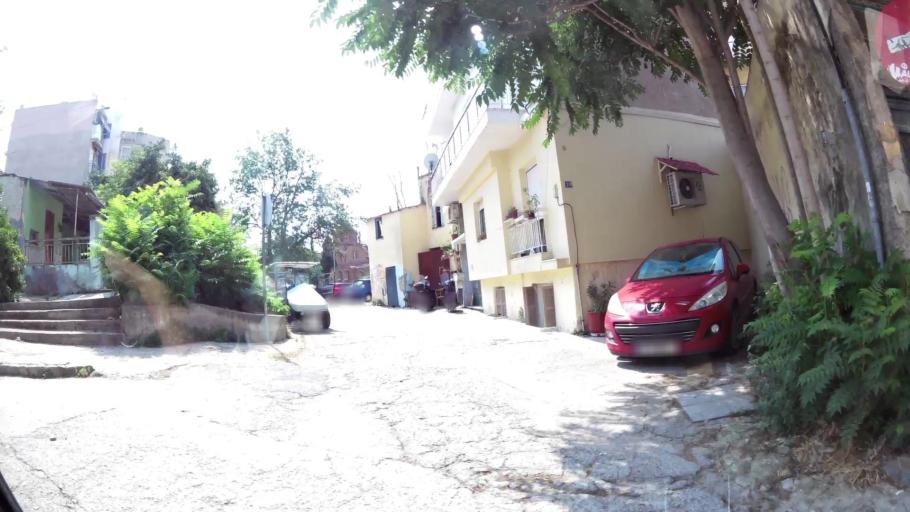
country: GR
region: Central Macedonia
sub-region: Nomos Thessalonikis
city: Sykies
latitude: 40.6436
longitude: 22.9436
